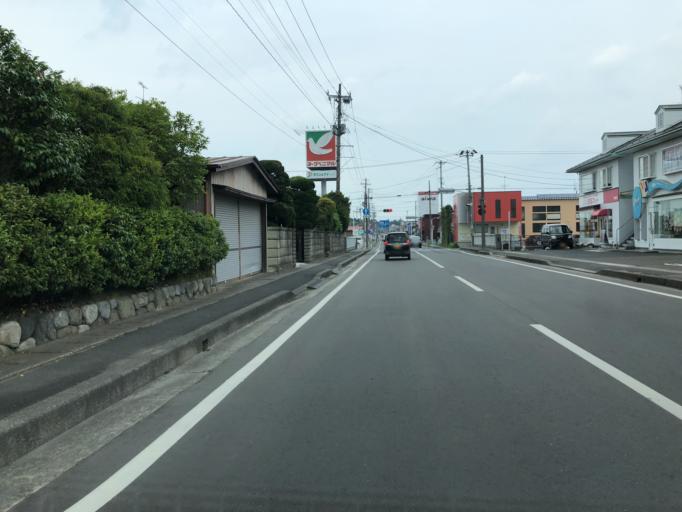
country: JP
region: Miyagi
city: Marumori
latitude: 37.8000
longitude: 140.9178
